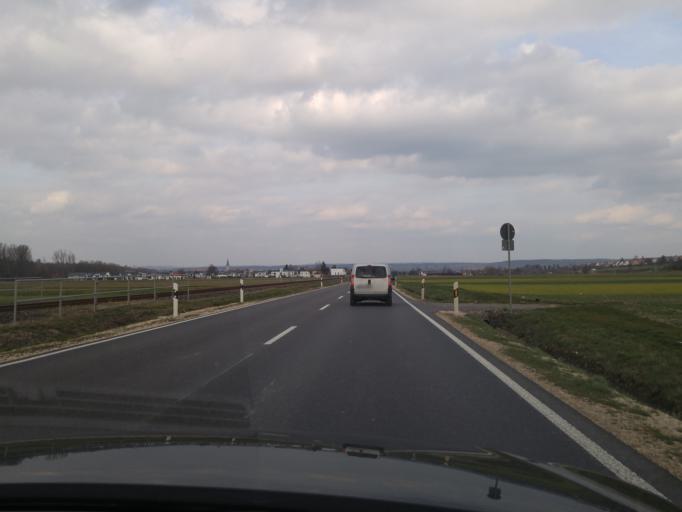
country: DE
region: Baden-Wuerttemberg
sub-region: Regierungsbezirk Stuttgart
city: Owen
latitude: 48.6016
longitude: 9.4506
